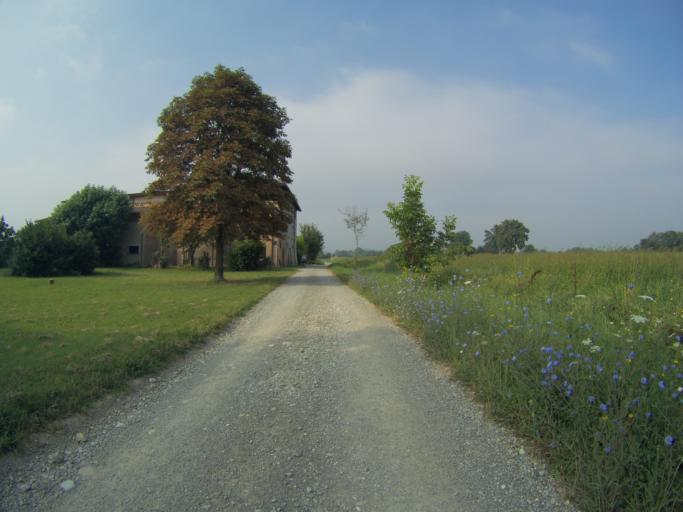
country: IT
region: Emilia-Romagna
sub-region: Provincia di Reggio Emilia
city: Albinea
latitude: 44.6397
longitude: 10.6185
